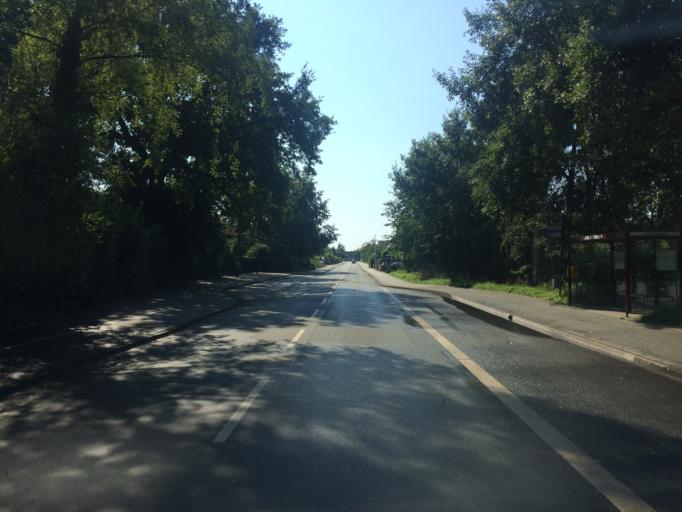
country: DE
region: North Rhine-Westphalia
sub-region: Regierungsbezirk Munster
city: Telgte
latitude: 52.0032
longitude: 7.7099
